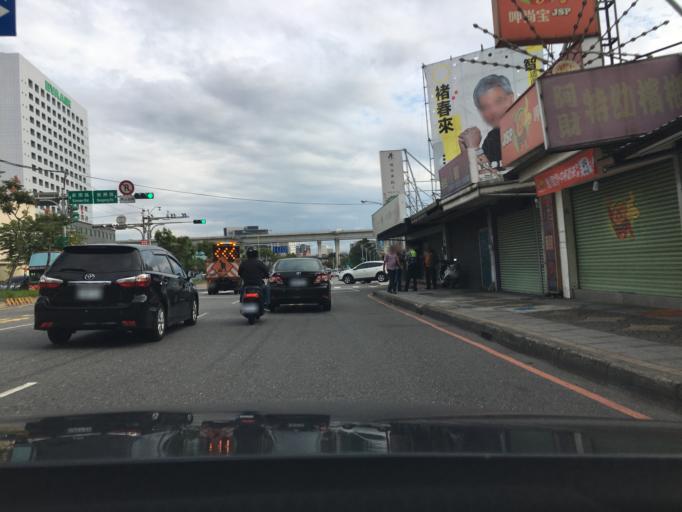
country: TW
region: Taiwan
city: Taoyuan City
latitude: 25.0413
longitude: 121.2953
